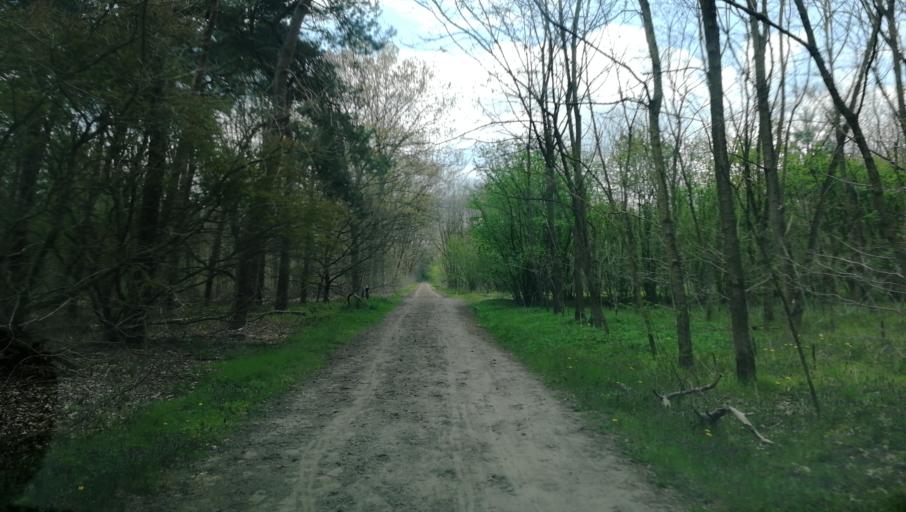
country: NL
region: Limburg
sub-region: Gemeente Peel en Maas
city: Maasbree
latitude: 51.4010
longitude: 5.9874
